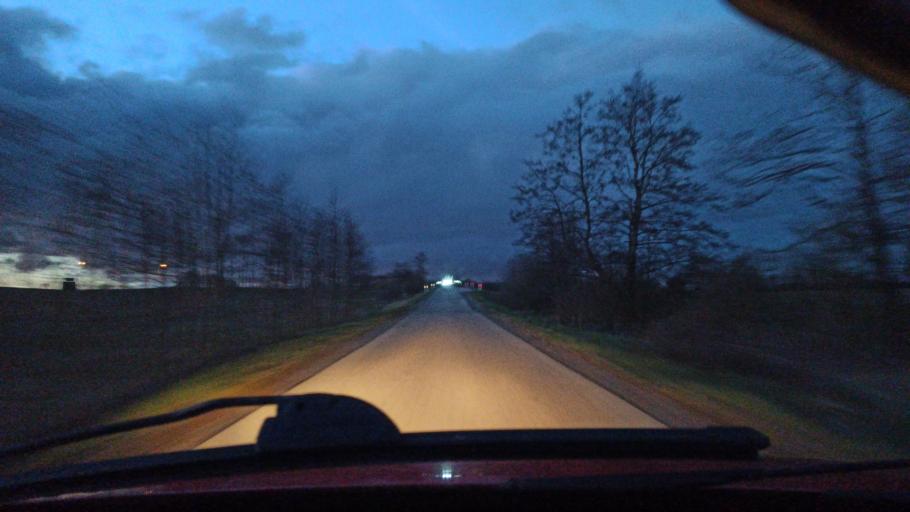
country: PL
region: Warmian-Masurian Voivodeship
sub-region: Powiat elblaski
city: Gronowo Gorne
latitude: 54.1689
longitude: 19.5354
